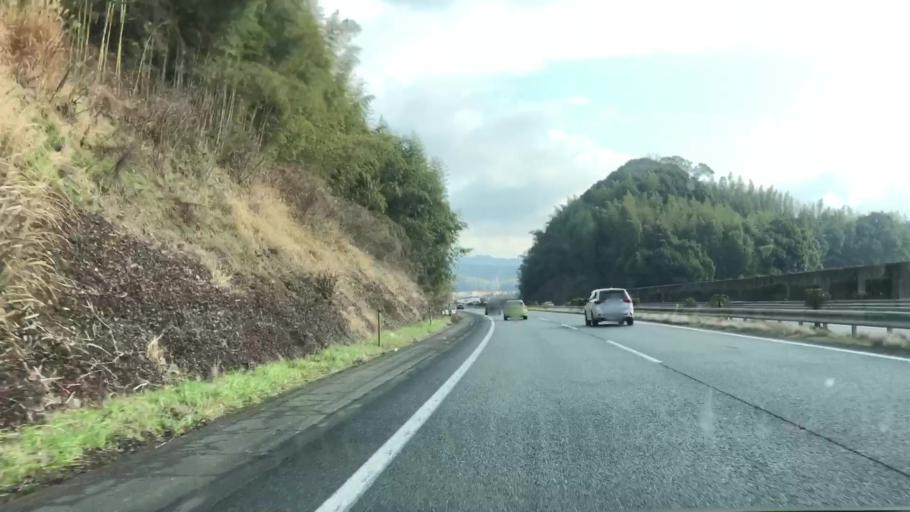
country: JP
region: Kumamoto
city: Tamana
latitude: 32.9981
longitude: 130.5931
